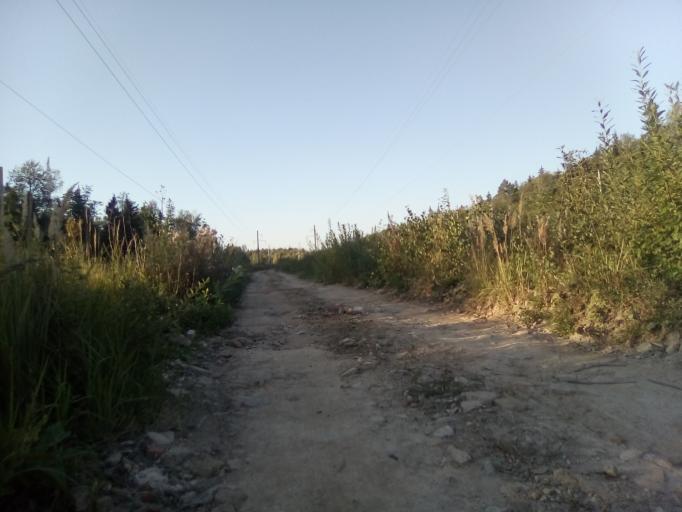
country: RU
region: Moskovskaya
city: Aprelevka
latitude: 55.5752
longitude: 37.0656
